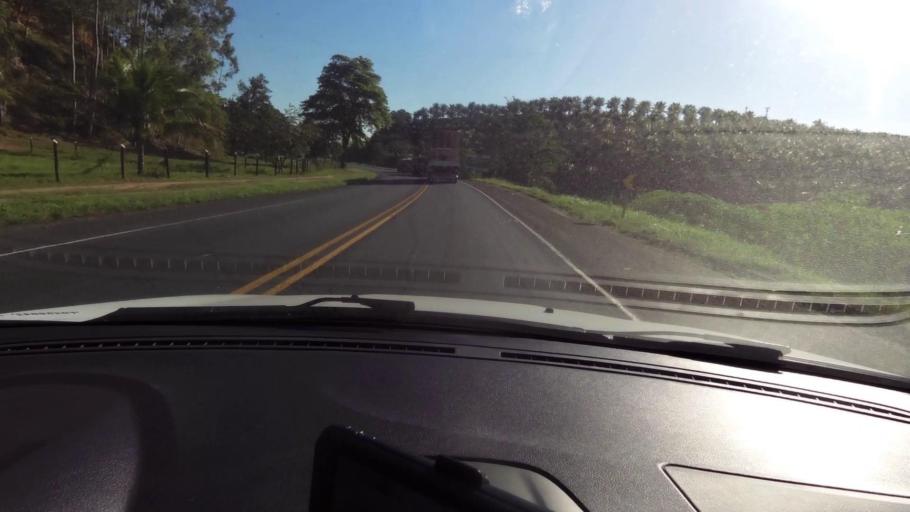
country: BR
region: Espirito Santo
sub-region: Alfredo Chaves
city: Alfredo Chaves
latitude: -20.6846
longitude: -40.6716
